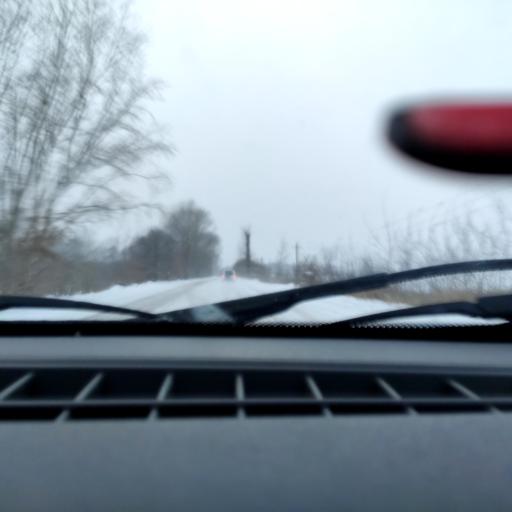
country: RU
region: Bashkortostan
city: Blagoveshchensk
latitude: 54.9109
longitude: 56.0046
